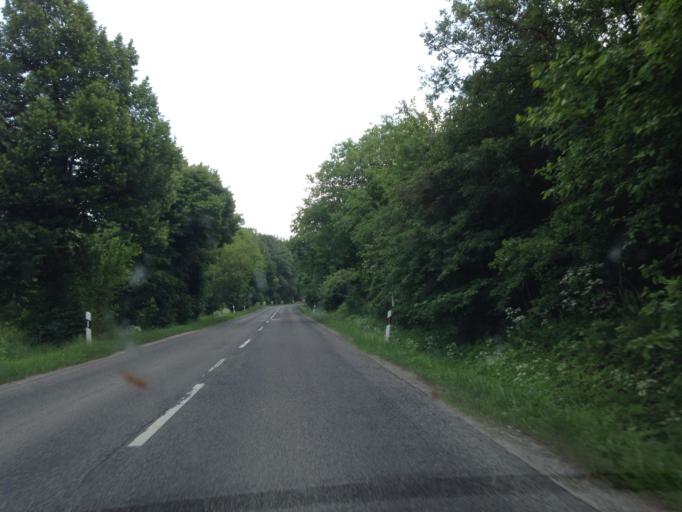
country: HU
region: Pest
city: Szob
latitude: 47.8008
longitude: 18.8556
